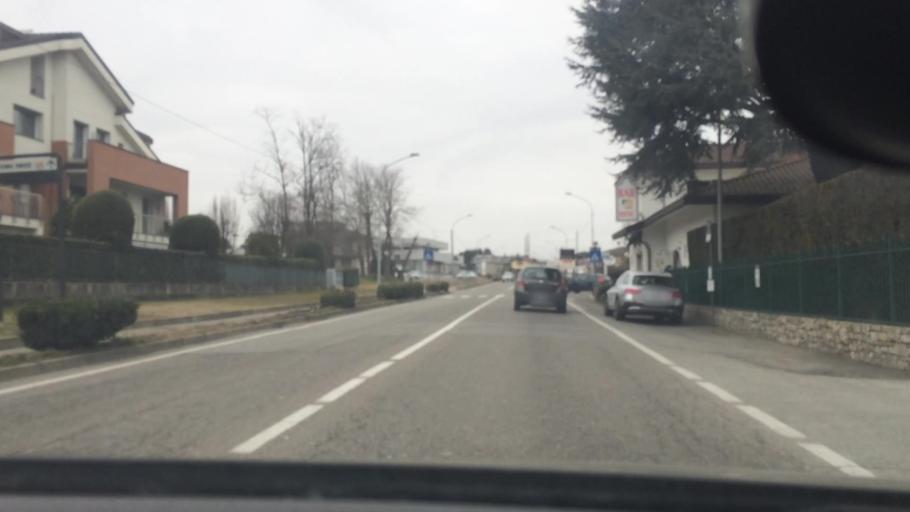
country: IT
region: Lombardy
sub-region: Provincia di Monza e Brianza
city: Lentate sul Seveso
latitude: 45.6809
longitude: 9.1130
